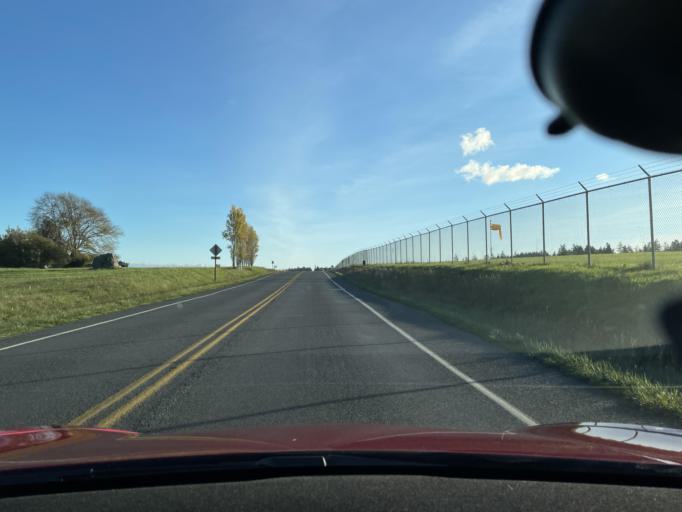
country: US
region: Washington
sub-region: San Juan County
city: Friday Harbor
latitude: 48.5214
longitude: -123.0231
